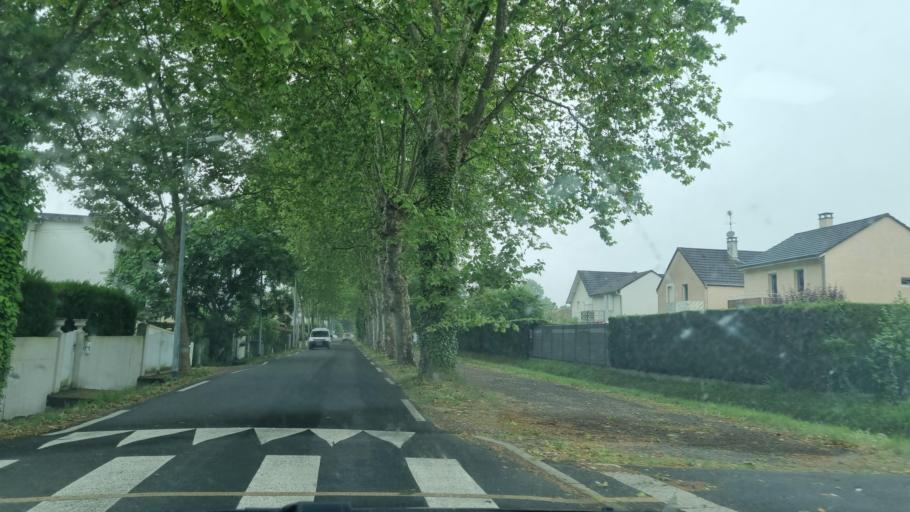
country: FR
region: Aquitaine
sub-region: Departement des Pyrenees-Atlantiques
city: Pau
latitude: 43.3261
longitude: -0.3383
